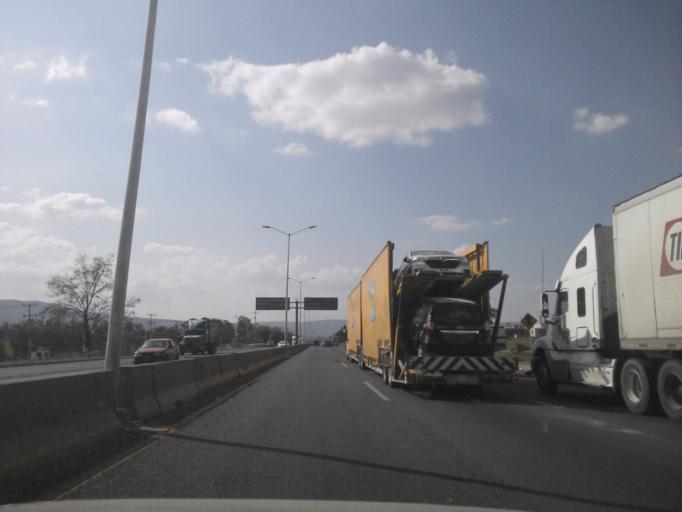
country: MX
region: Jalisco
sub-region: Tlajomulco de Zuniga
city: La Tijera
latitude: 20.6088
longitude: -103.4084
